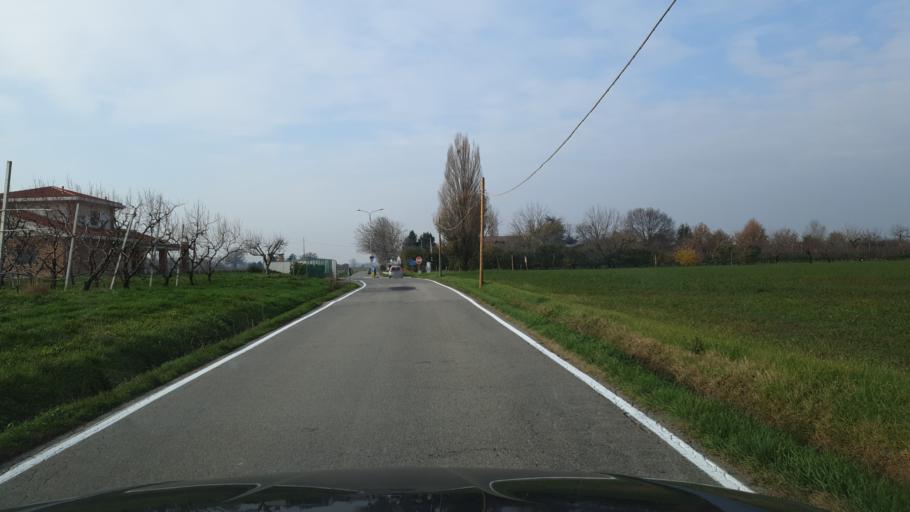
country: IT
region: Emilia-Romagna
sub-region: Provincia di Bologna
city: Crespellano
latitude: 44.5227
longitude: 11.1193
